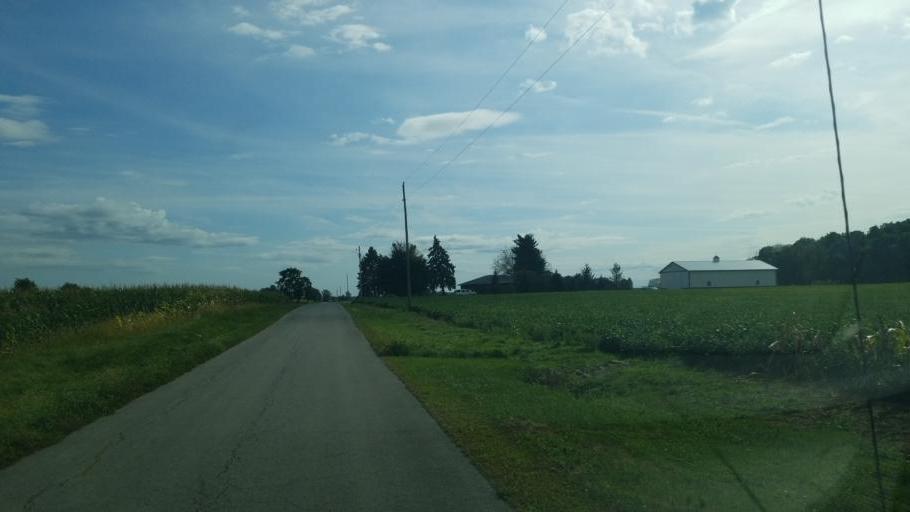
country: US
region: Ohio
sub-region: Hancock County
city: Arlington
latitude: 40.8564
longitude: -83.5760
